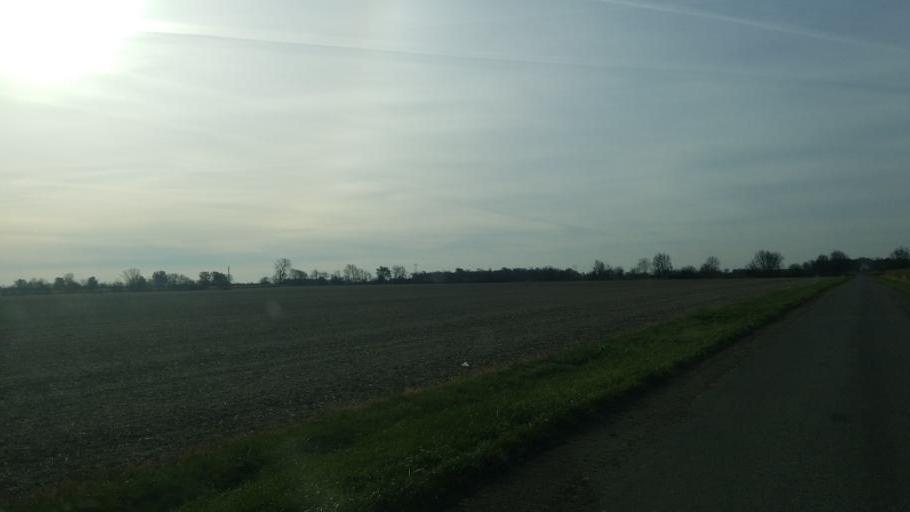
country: US
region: Ohio
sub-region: Union County
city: Marysville
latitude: 40.1431
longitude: -83.3633
